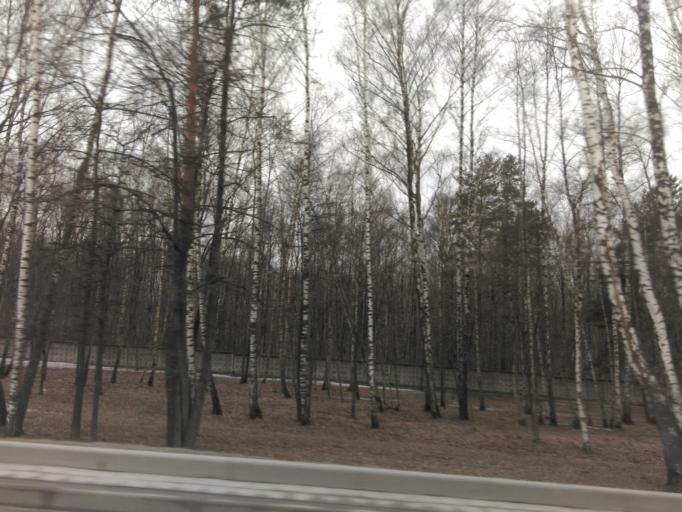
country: RU
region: Moskovskaya
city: Bol'shaya Setun'
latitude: 55.7558
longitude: 37.3989
